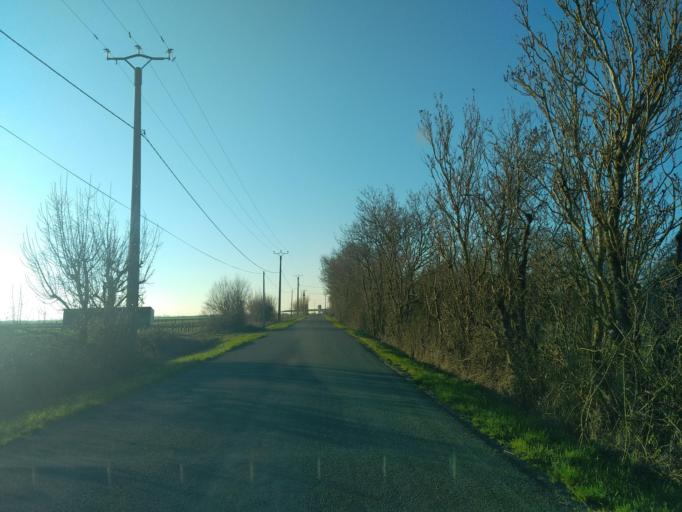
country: FR
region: Pays de la Loire
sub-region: Departement de la Vendee
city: Triaize
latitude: 46.3882
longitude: -1.2710
